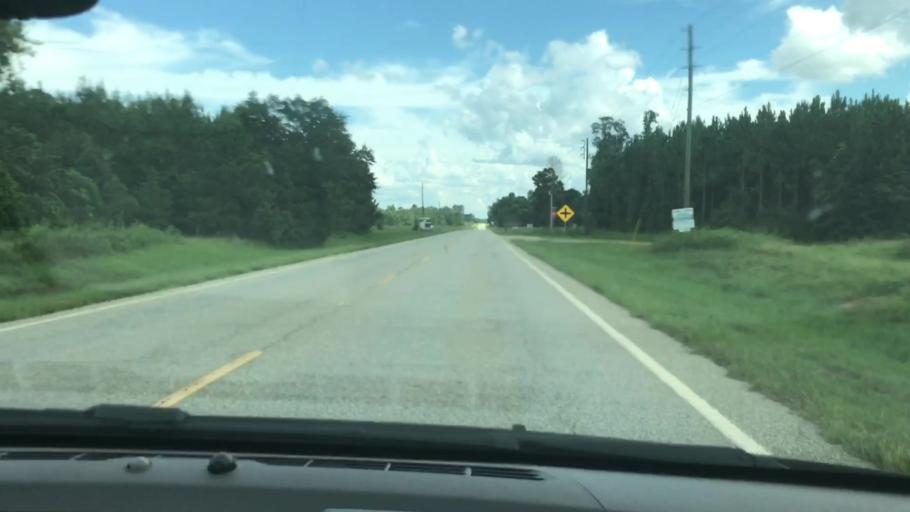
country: US
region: Georgia
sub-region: Quitman County
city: Georgetown
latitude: 31.7613
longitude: -85.0756
